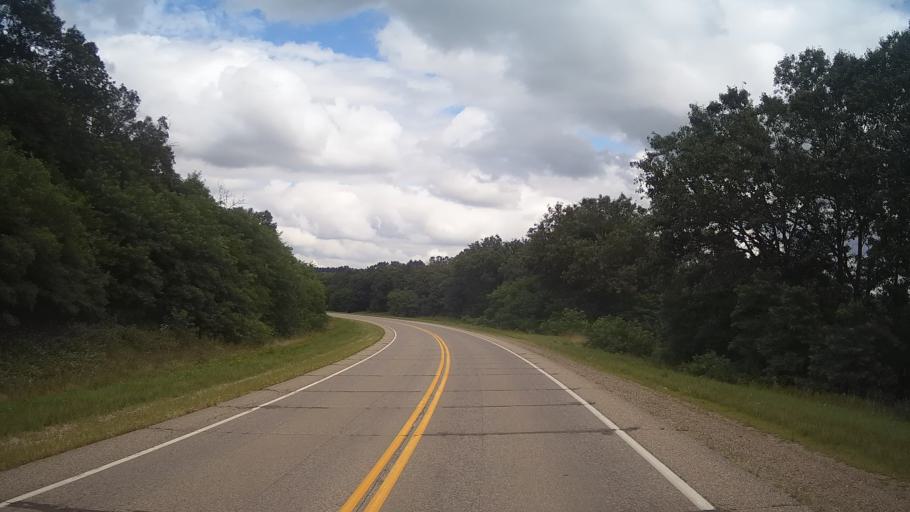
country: US
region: Wisconsin
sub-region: Marquette County
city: Westfield
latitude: 44.0242
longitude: -89.5413
